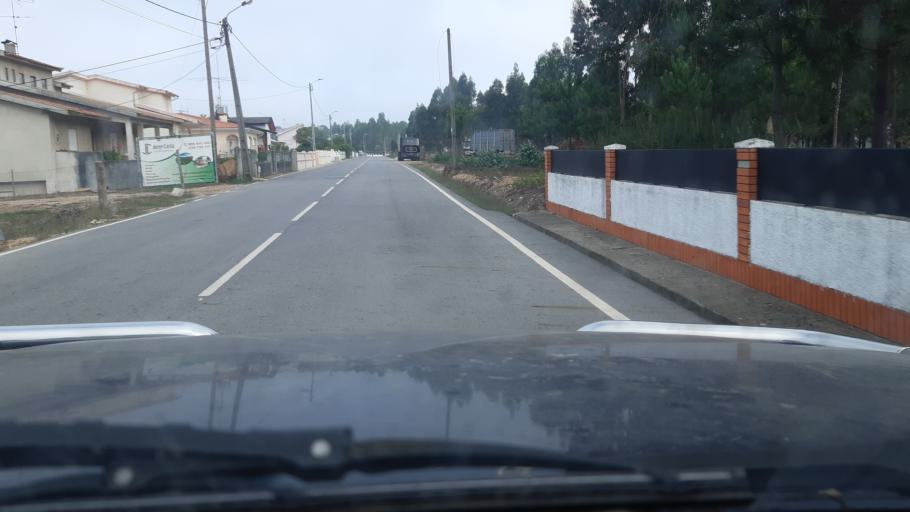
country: PT
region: Aveiro
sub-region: Agueda
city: Agueda
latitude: 40.5826
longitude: -8.4563
